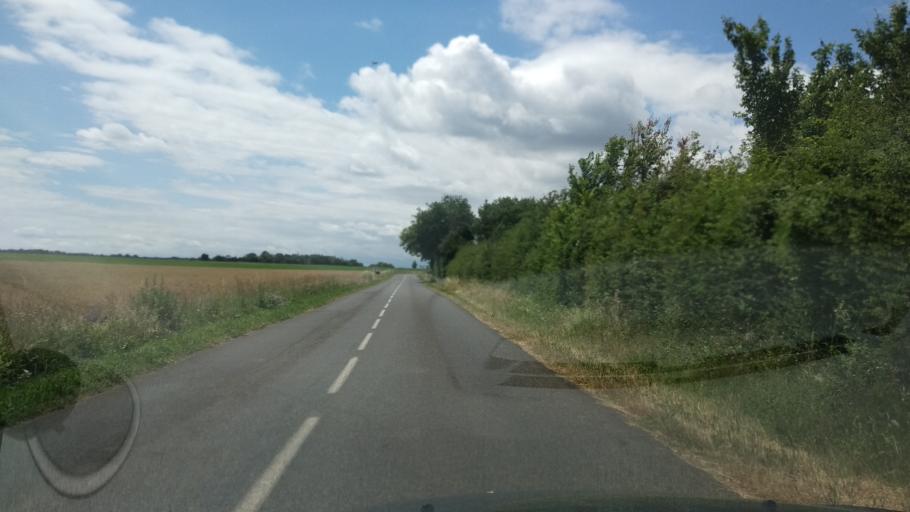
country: FR
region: Poitou-Charentes
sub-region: Departement de la Vienne
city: Vouneuil-sous-Biard
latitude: 46.6065
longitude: 0.2684
